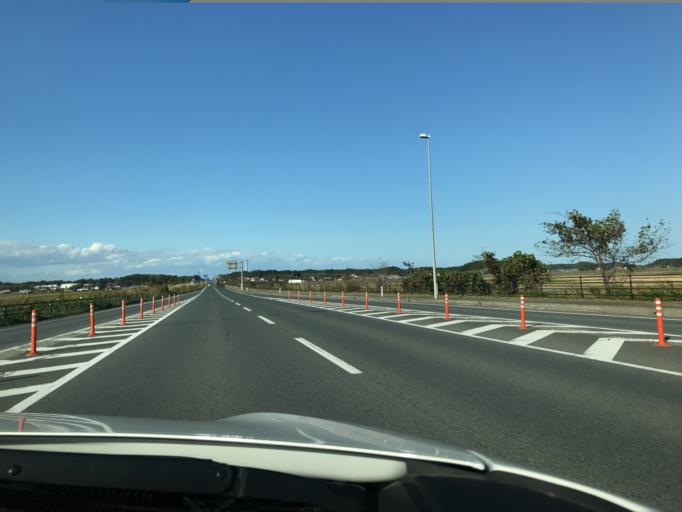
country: JP
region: Miyagi
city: Marumori
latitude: 37.7927
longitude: 140.9440
